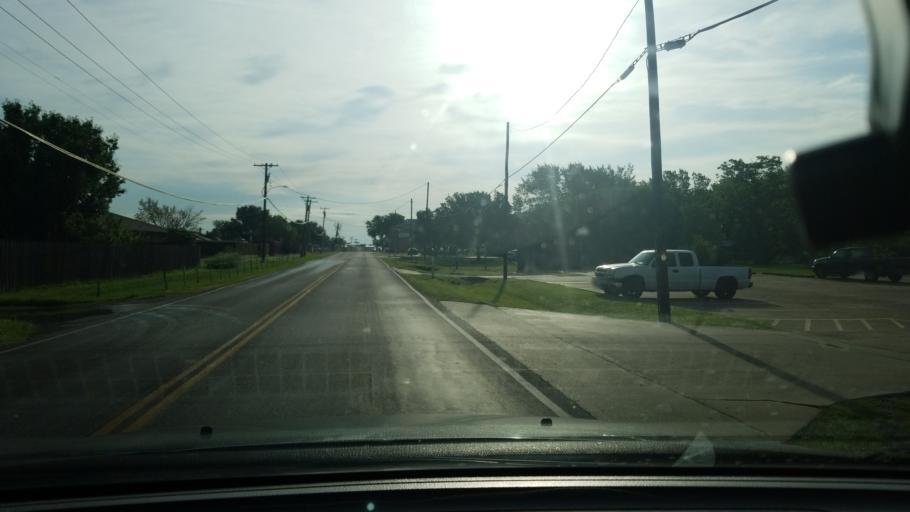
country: US
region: Texas
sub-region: Dallas County
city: Mesquite
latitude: 32.7957
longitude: -96.6151
